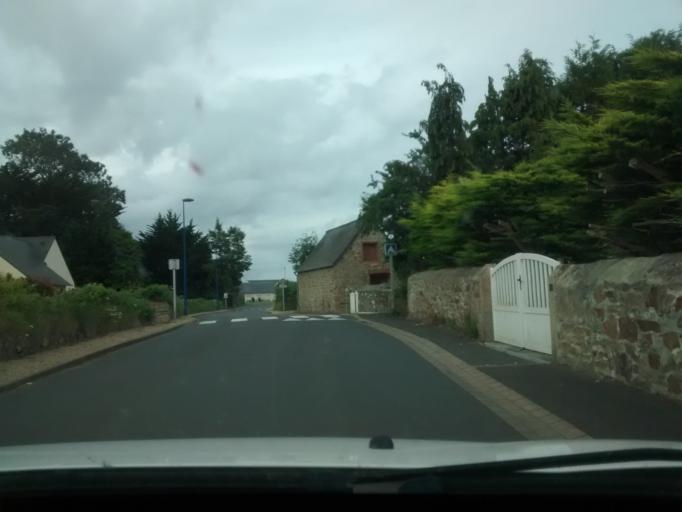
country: FR
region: Brittany
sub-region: Departement des Cotes-d'Armor
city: Louannec
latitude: 48.7960
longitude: -3.4072
